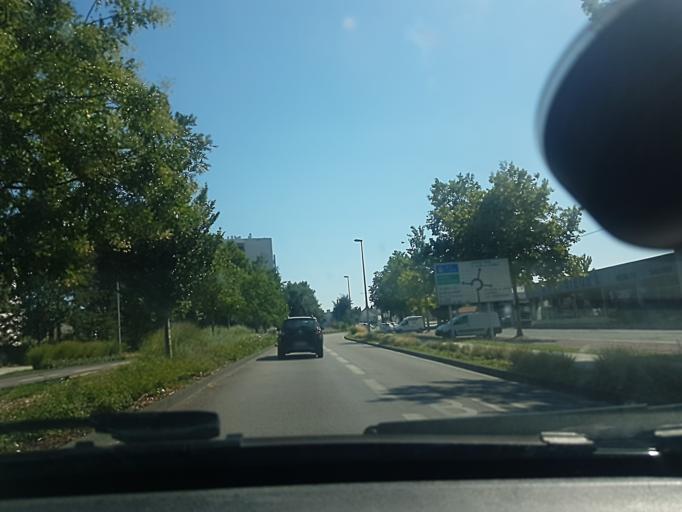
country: FR
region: Bourgogne
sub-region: Departement de Saone-et-Loire
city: Chalon-sur-Saone
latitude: 46.7921
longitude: 4.8632
